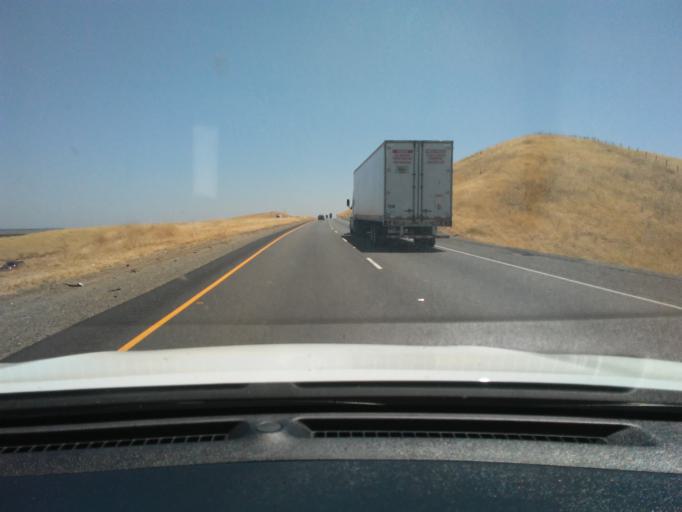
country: US
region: California
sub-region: Stanislaus County
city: Patterson
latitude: 37.4369
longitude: -121.1612
